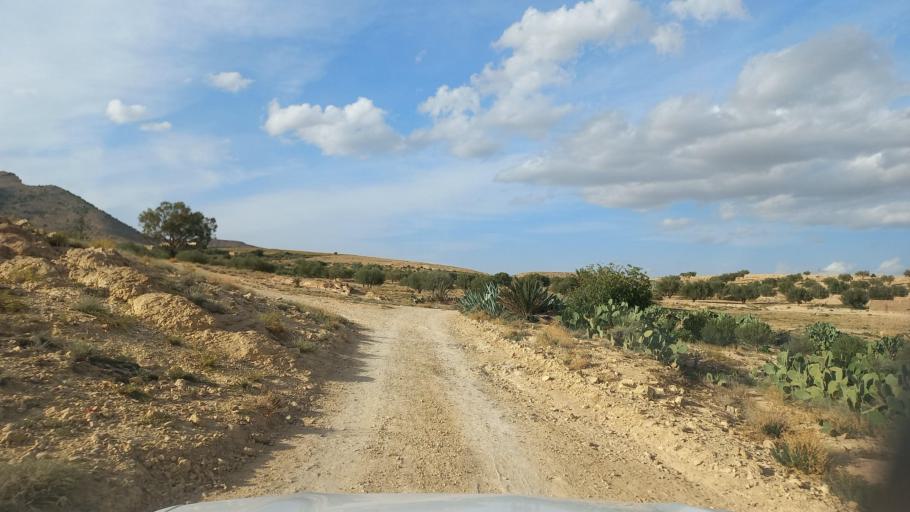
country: TN
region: Al Qasrayn
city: Sbiba
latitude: 35.4531
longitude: 9.0834
